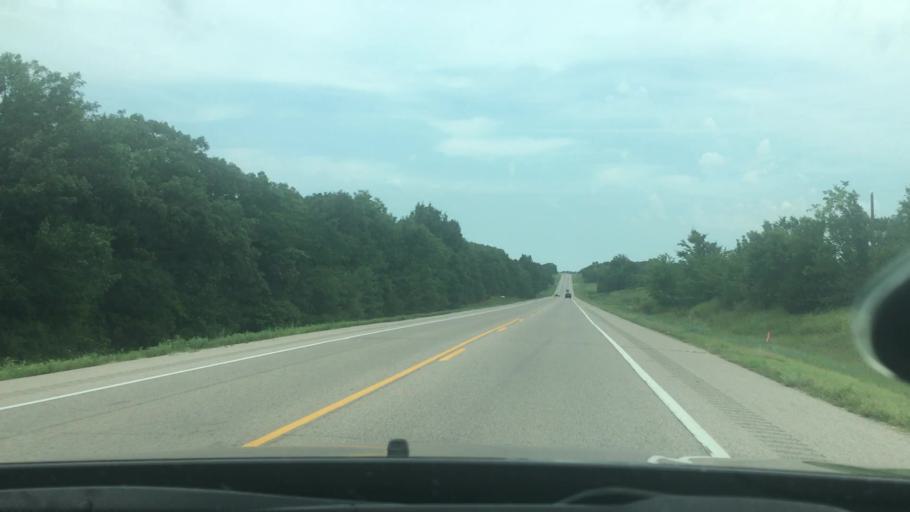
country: US
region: Oklahoma
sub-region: Seminole County
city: Konawa
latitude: 35.0028
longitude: -96.6788
